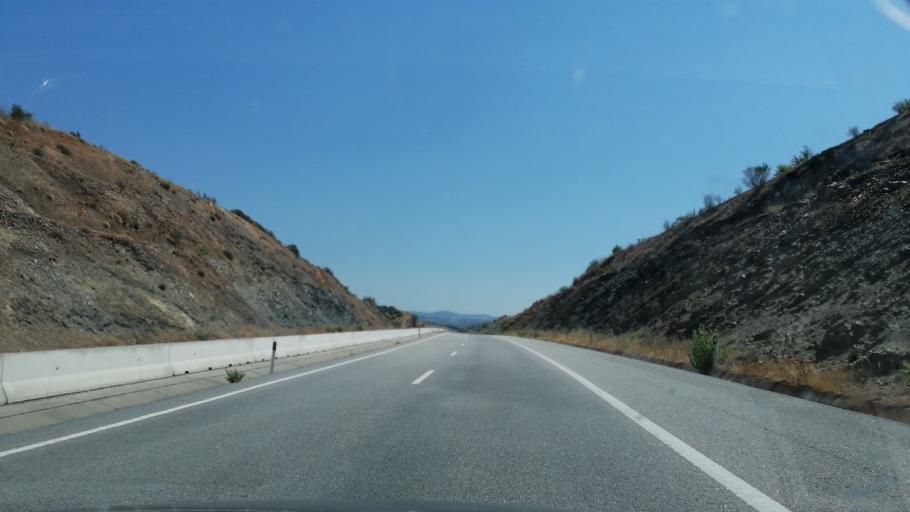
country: PT
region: Braganca
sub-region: Mirandela
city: Mirandela
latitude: 41.5216
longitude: -7.1047
